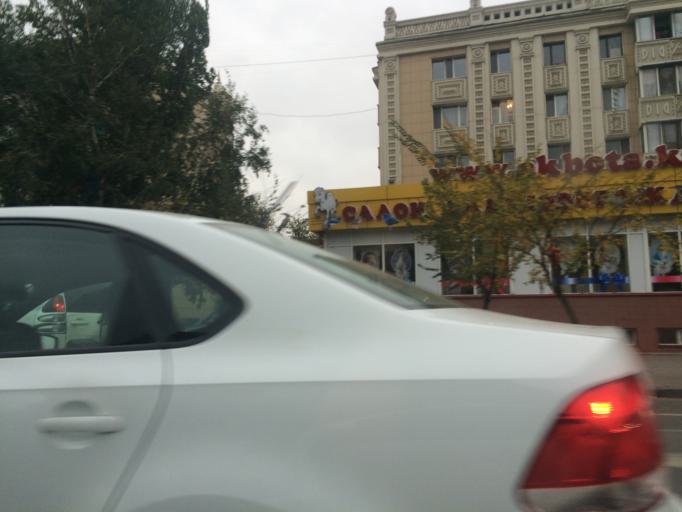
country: KZ
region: Astana Qalasy
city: Astana
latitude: 51.1665
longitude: 71.4269
